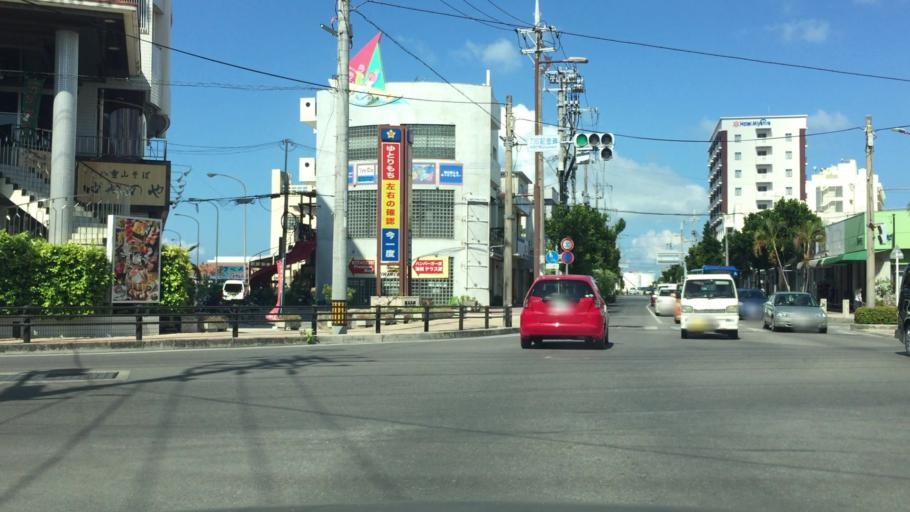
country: JP
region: Okinawa
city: Ishigaki
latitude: 24.3382
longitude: 124.1579
